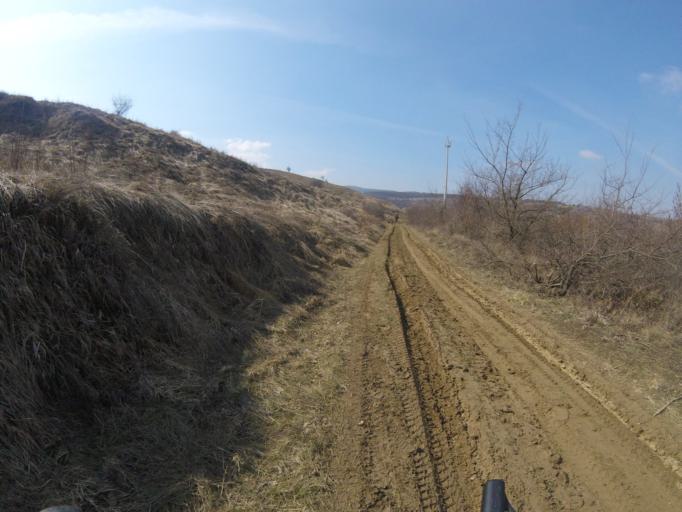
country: HU
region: Komarom-Esztergom
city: Nyergesujfalu
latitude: 47.7482
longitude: 18.5534
